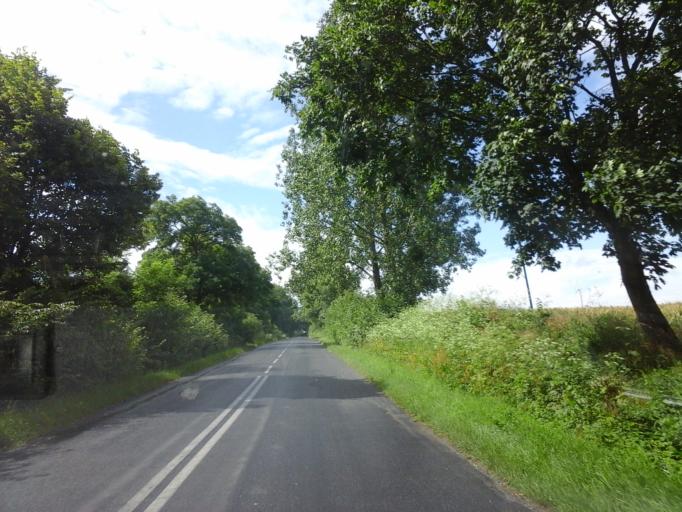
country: PL
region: West Pomeranian Voivodeship
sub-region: Powiat choszczenski
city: Choszczno
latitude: 53.1289
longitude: 15.4537
